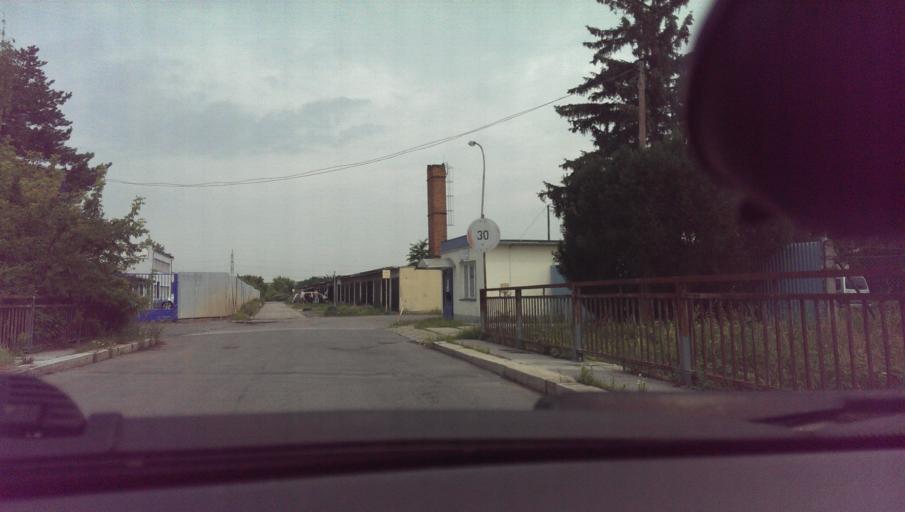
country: CZ
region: Zlin
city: Tecovice
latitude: 49.2090
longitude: 17.5789
